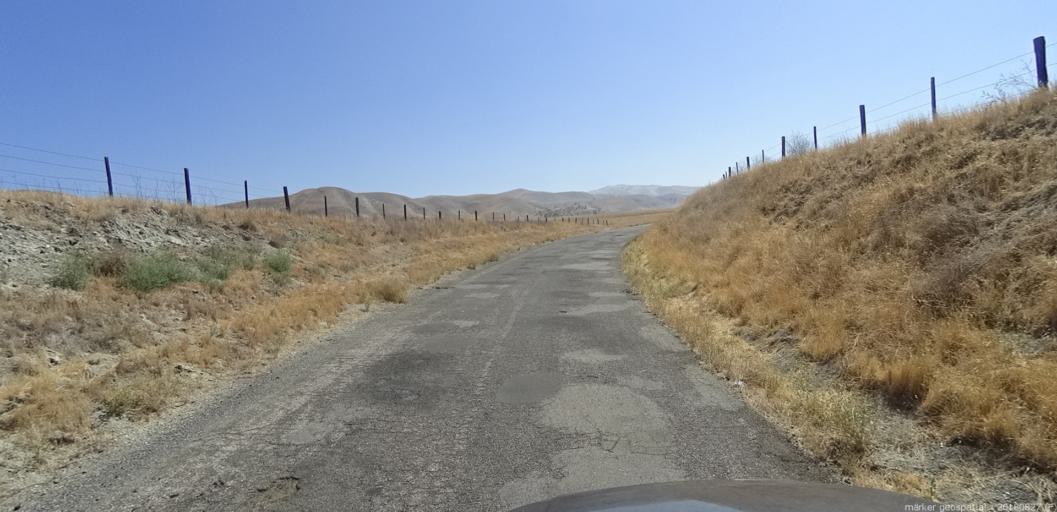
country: US
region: California
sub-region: Monterey County
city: King City
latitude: 36.2953
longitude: -120.9870
